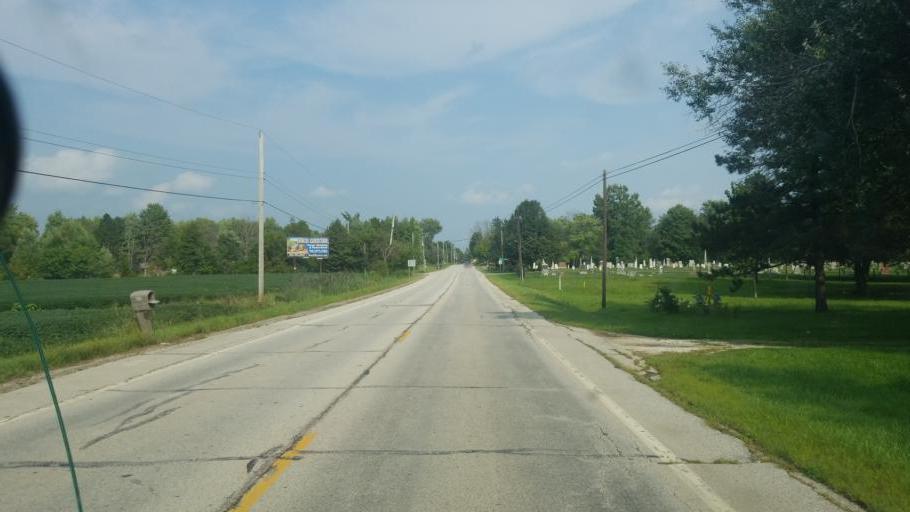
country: US
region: Ohio
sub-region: Medina County
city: Medina
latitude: 41.1673
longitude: -81.9333
